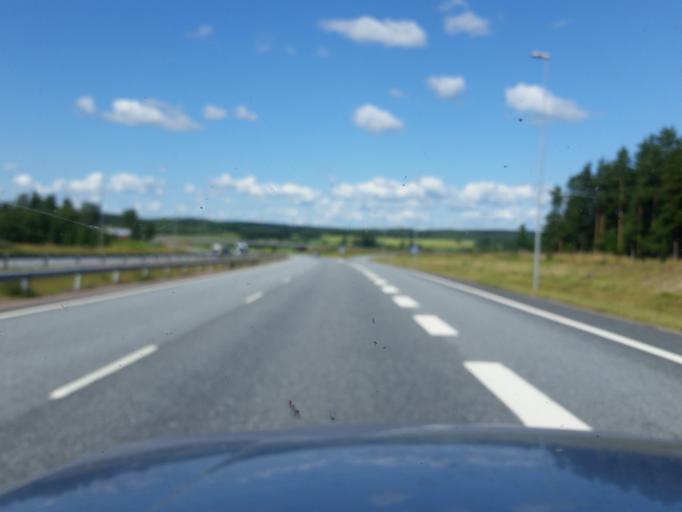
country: FI
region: Varsinais-Suomi
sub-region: Salo
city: Suomusjaervi
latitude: 60.3869
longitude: 23.5941
